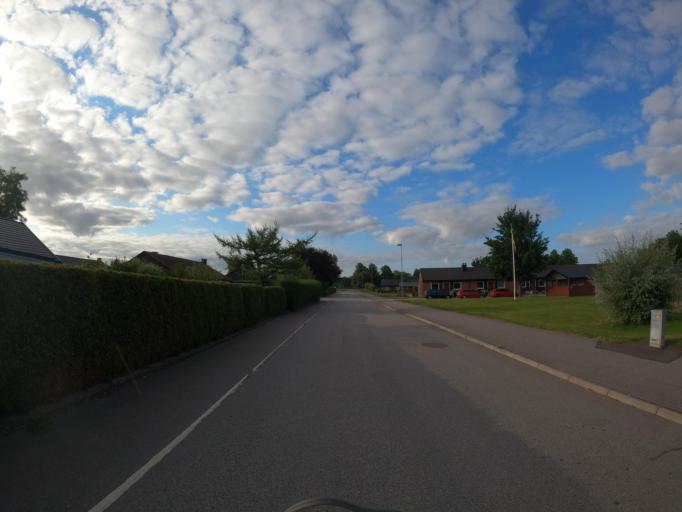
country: SE
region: Skane
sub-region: Staffanstorps Kommun
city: Staffanstorp
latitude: 55.6507
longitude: 13.2150
